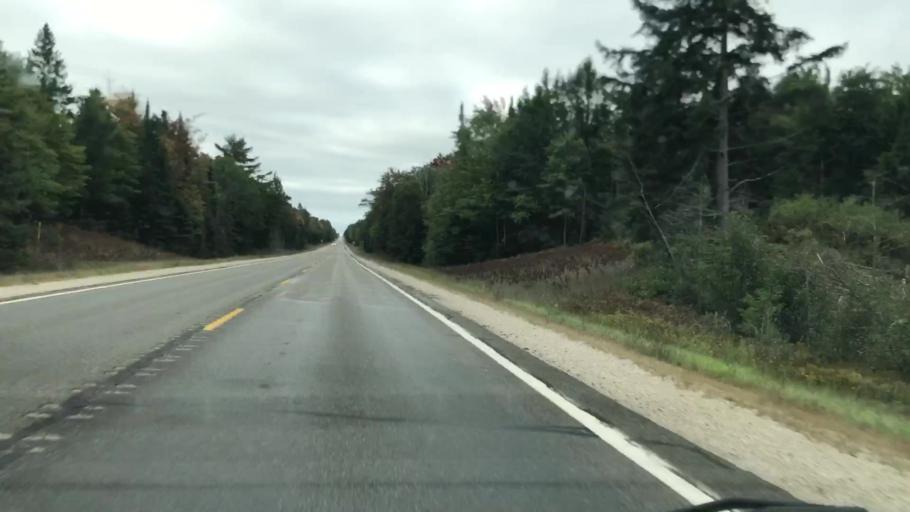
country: US
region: Michigan
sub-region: Luce County
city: Newberry
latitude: 46.2359
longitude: -85.5722
